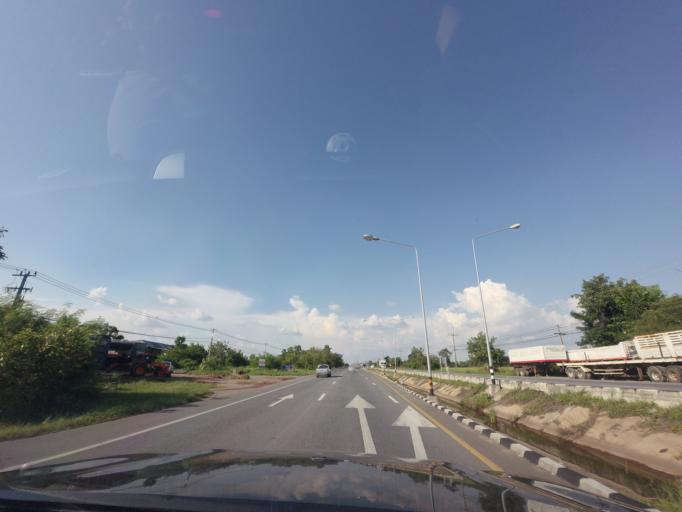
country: TH
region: Khon Kaen
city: Non Sila
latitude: 15.9825
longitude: 102.6963
